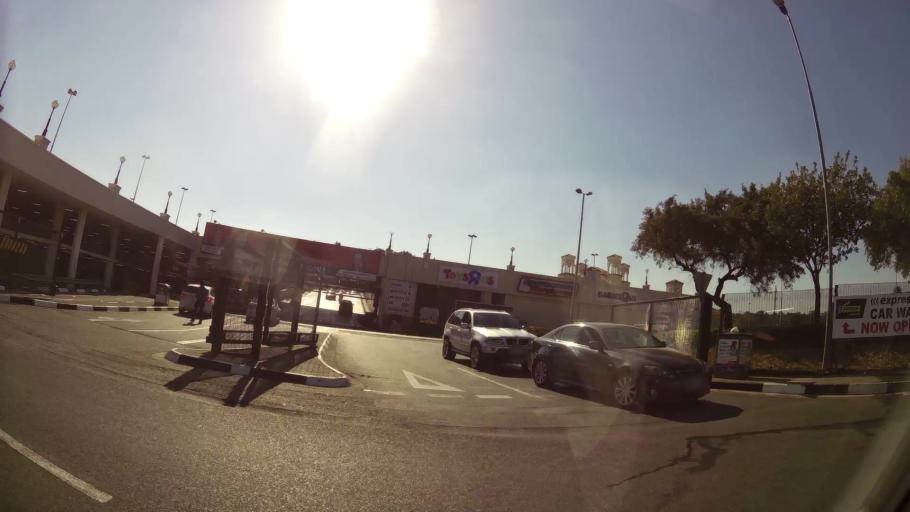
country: ZA
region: Gauteng
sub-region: City of Johannesburg Metropolitan Municipality
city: Johannesburg
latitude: -26.2688
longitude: 28.0509
